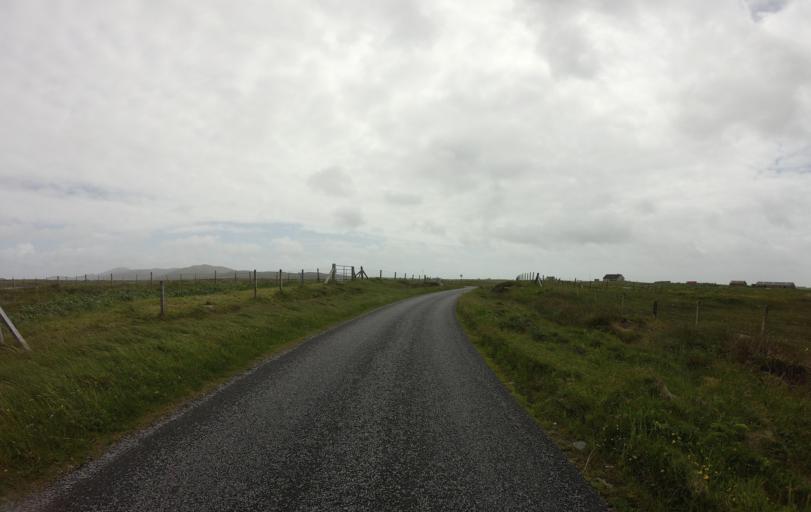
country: GB
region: Scotland
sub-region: Eilean Siar
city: Isle of South Uist
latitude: 57.2560
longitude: -7.4043
